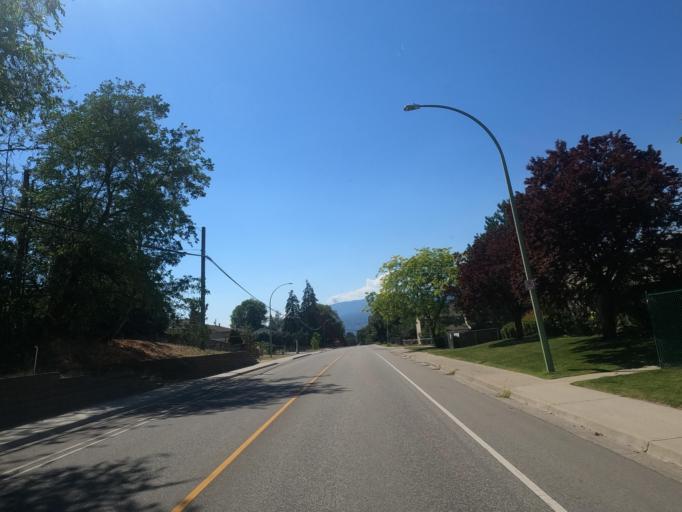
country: CA
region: British Columbia
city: Kelowna
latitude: 49.8863
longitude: -119.4643
